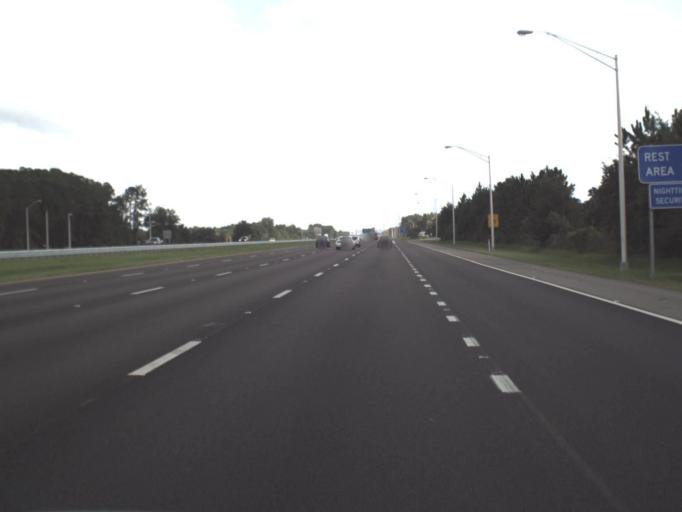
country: US
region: Florida
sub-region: Pasco County
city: Wesley Chapel
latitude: 28.2127
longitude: -82.3723
